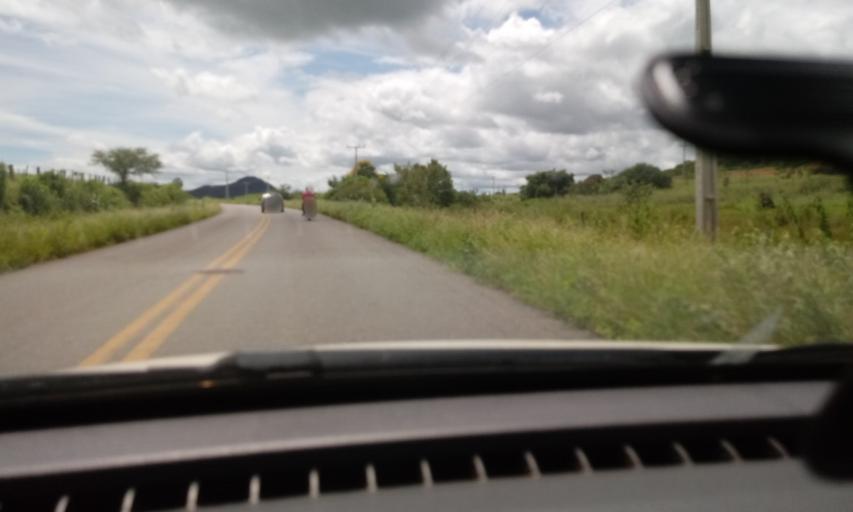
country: BR
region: Bahia
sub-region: Guanambi
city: Guanambi
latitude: -14.1408
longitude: -42.8448
